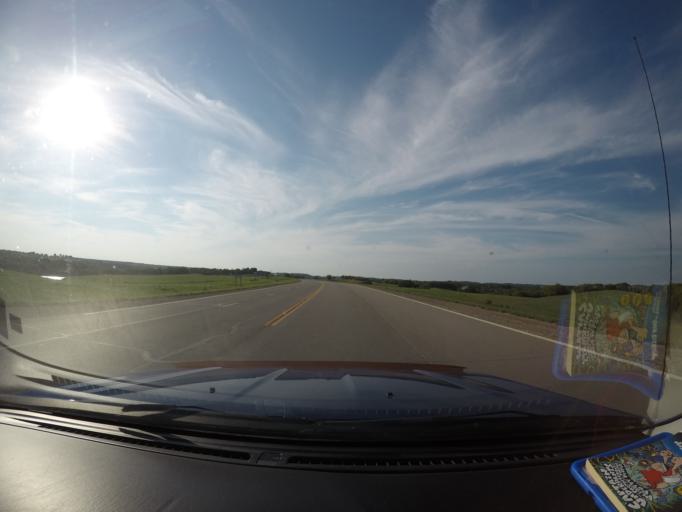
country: US
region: Kansas
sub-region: Atchison County
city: Atchison
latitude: 39.4707
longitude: -95.0971
